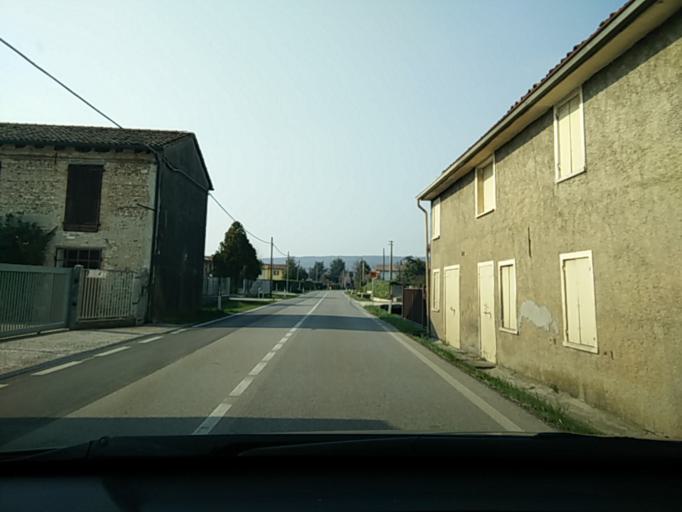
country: IT
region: Veneto
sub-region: Provincia di Treviso
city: Selva del Montello
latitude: 45.7721
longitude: 12.1441
